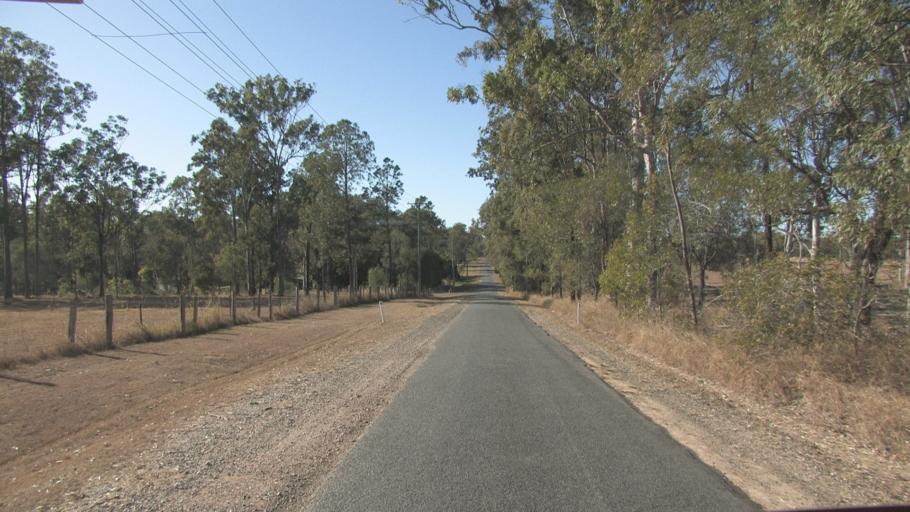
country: AU
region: Queensland
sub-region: Logan
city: Cedar Vale
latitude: -27.8471
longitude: 153.0121
